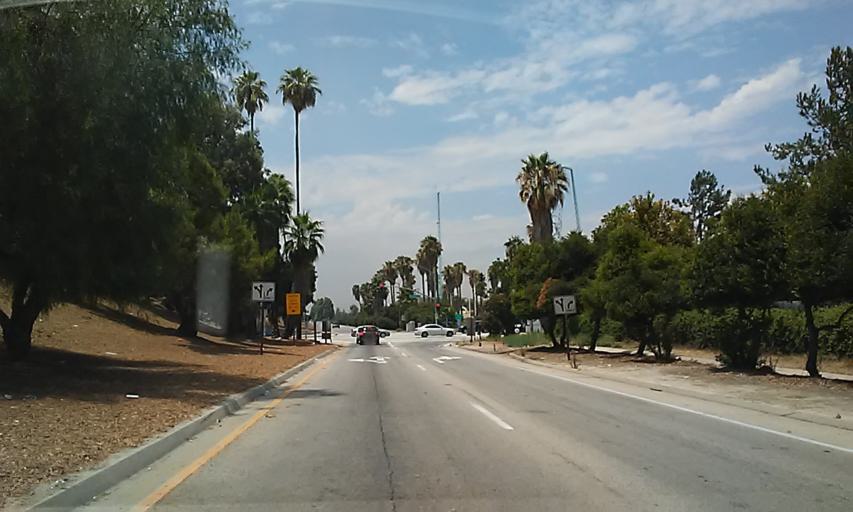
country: US
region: California
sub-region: San Bernardino County
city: Loma Linda
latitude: 34.0670
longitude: -117.2252
